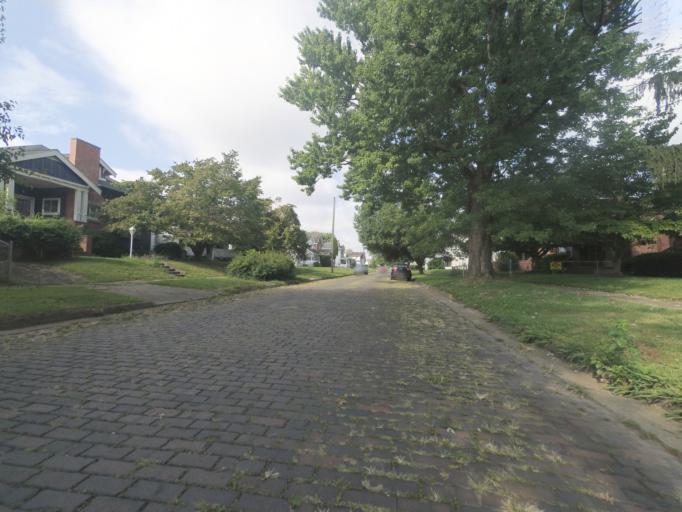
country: US
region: West Virginia
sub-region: Cabell County
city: Huntington
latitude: 38.4324
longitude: -82.4054
